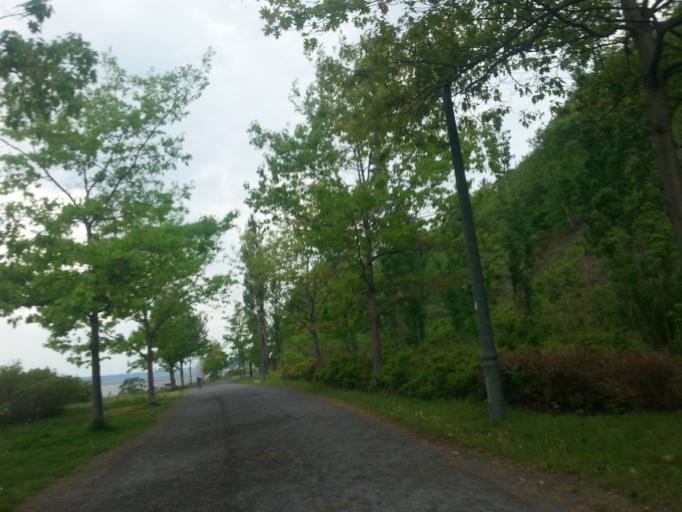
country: CA
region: Quebec
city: L'Ancienne-Lorette
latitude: 46.7488
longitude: -71.3277
